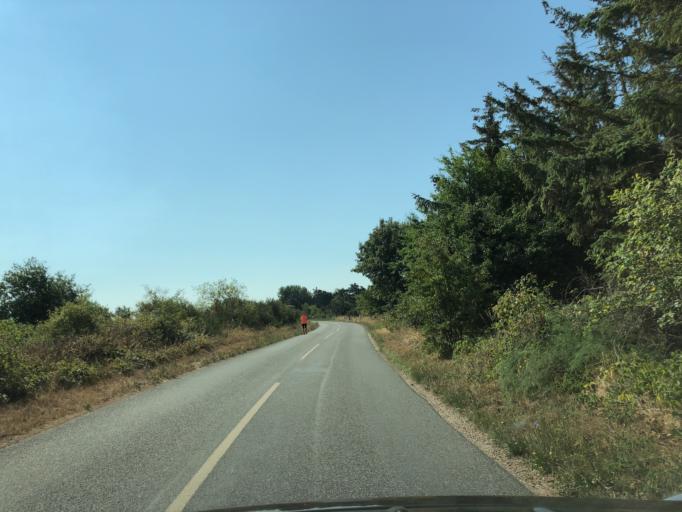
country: DK
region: Zealand
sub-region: Odsherred Kommune
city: Asnaes
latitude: 55.9961
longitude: 11.2899
